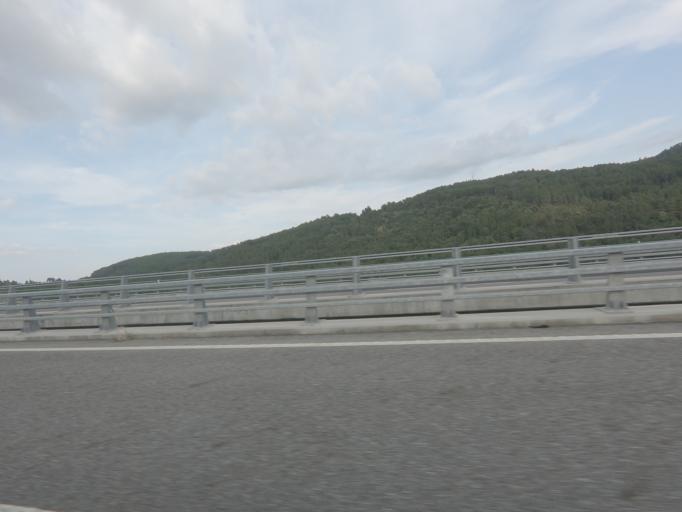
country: PT
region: Vila Real
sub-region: Boticas
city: Boticas
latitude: 41.6830
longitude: -7.5659
